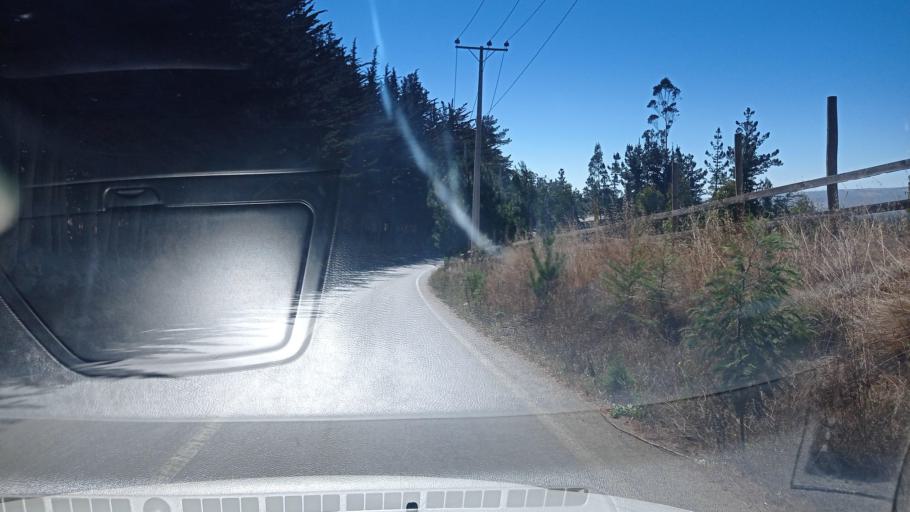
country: CL
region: O'Higgins
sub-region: Provincia de Colchagua
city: Santa Cruz
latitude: -34.4195
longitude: -72.0009
